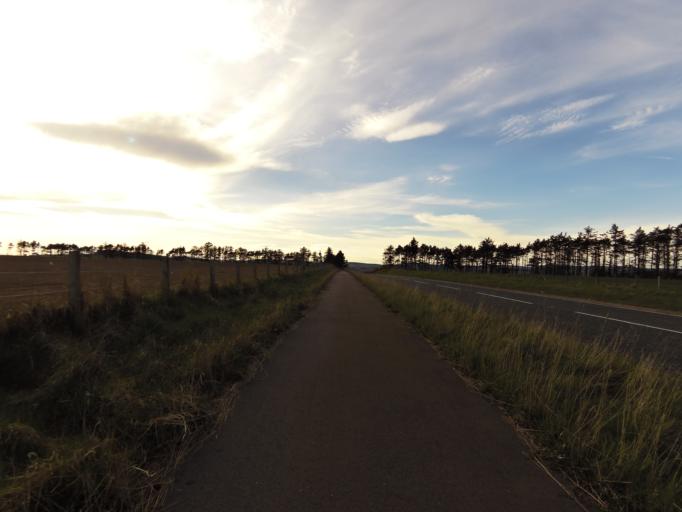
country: GB
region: Scotland
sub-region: Aberdeenshire
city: Stonehaven
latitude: 56.9465
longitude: -2.2156
